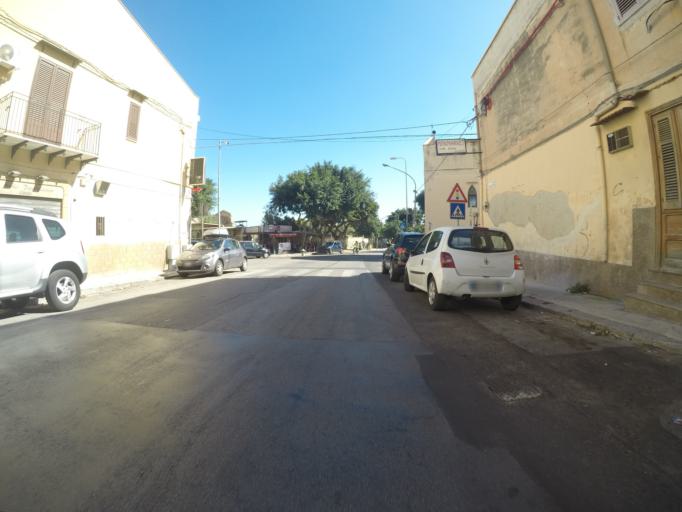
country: IT
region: Sicily
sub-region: Palermo
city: Palermo
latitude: 38.1655
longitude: 13.3671
